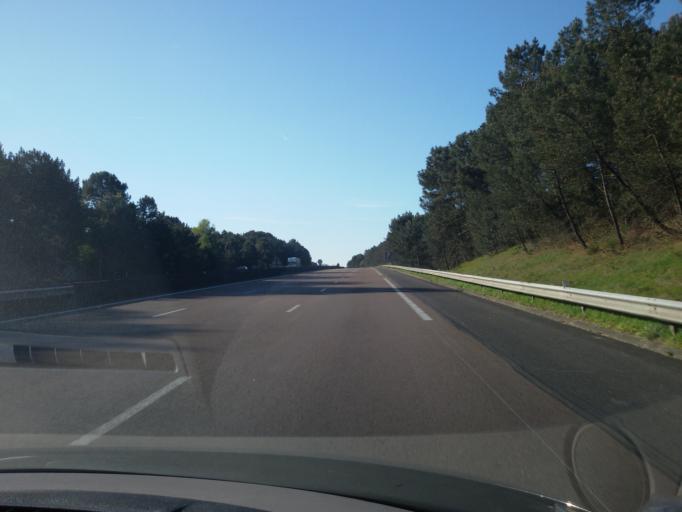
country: FR
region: Ile-de-France
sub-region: Departement de Seine-et-Marne
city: Arbonne-la-Foret
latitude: 48.3857
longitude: 2.5572
